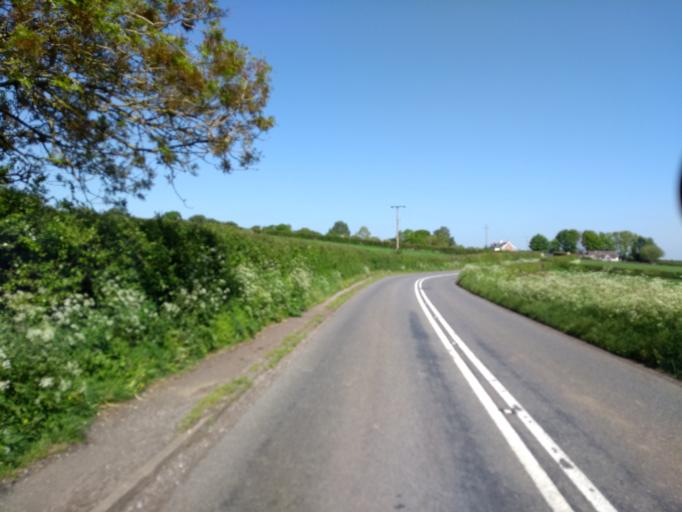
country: GB
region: England
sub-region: Somerset
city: Chard
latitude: 50.8601
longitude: -2.9590
